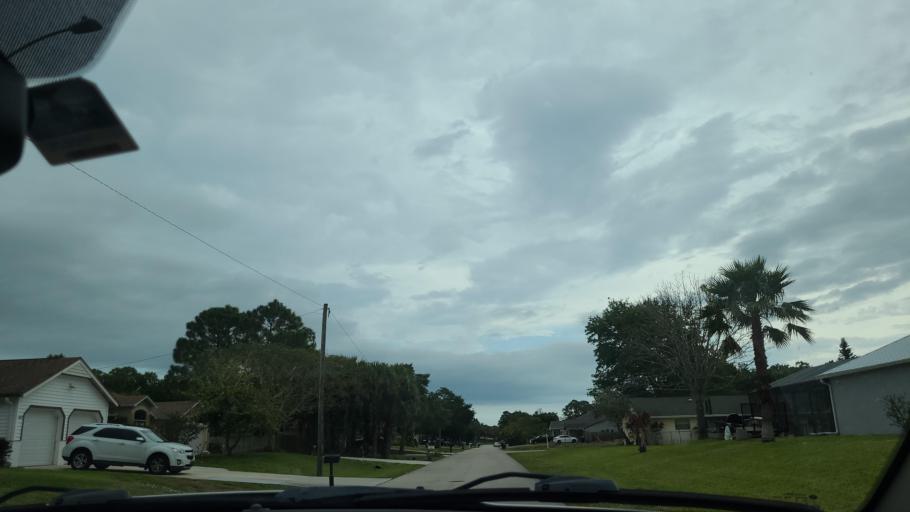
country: US
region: Florida
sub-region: Brevard County
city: West Melbourne
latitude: 28.0125
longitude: -80.6610
